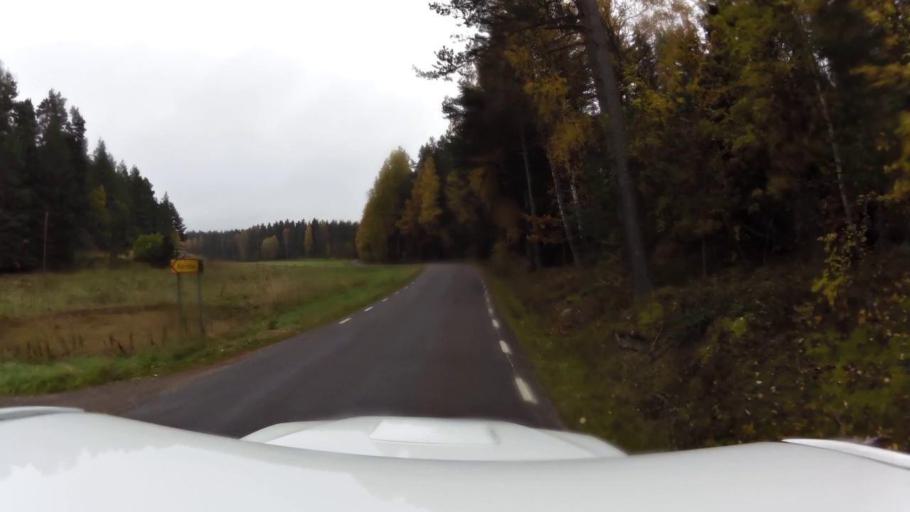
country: SE
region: OEstergoetland
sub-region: Linkopings Kommun
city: Linghem
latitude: 58.3543
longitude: 15.8541
